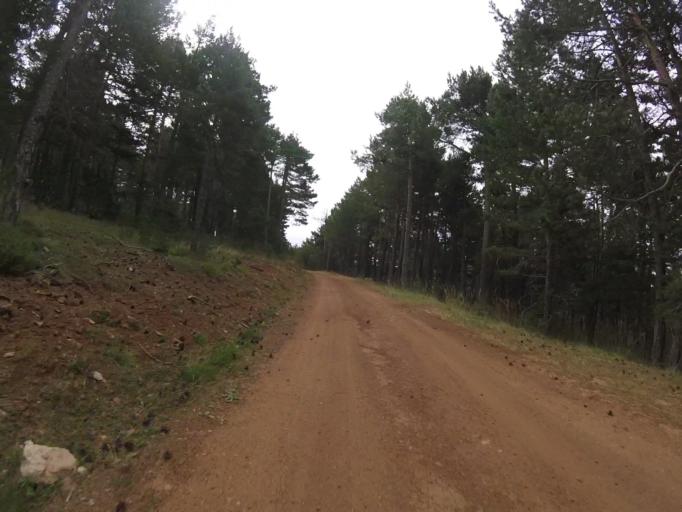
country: ES
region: Aragon
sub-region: Provincia de Teruel
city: Valdelinares
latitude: 40.3587
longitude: -0.6056
